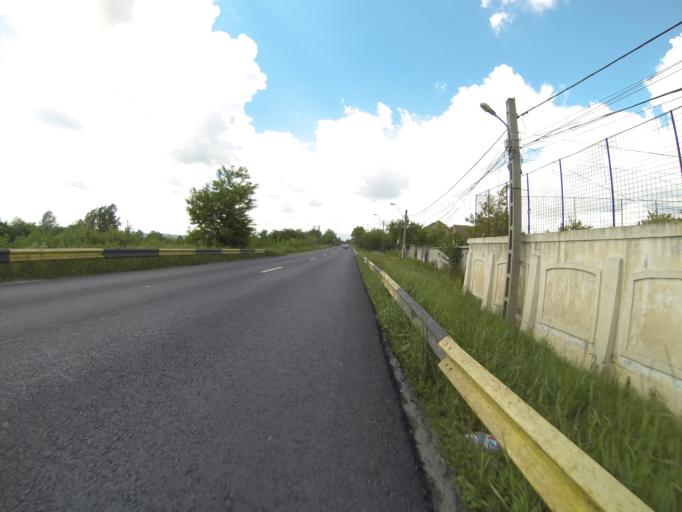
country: RO
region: Dolj
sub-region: Municipiul Craiova
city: Facai
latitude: 44.2706
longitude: 23.8209
